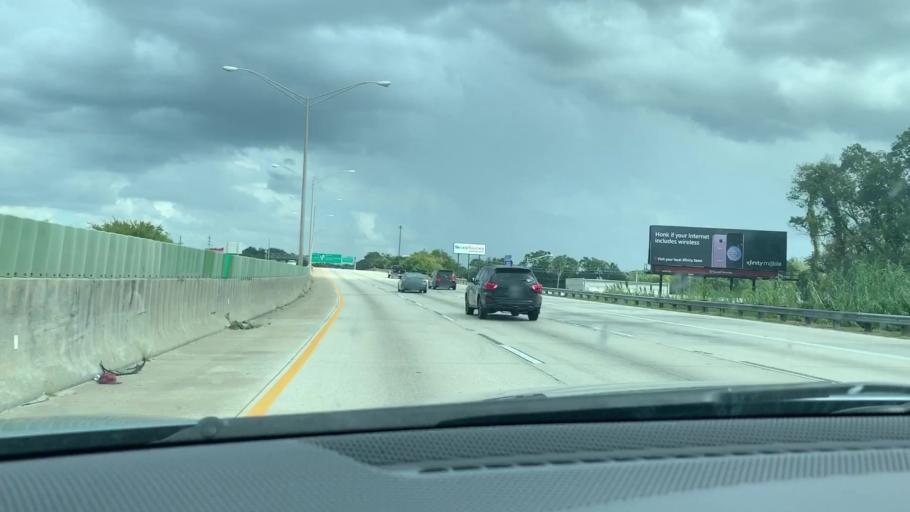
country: US
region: Florida
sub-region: Duval County
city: Jacksonville
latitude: 30.3180
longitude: -81.7277
